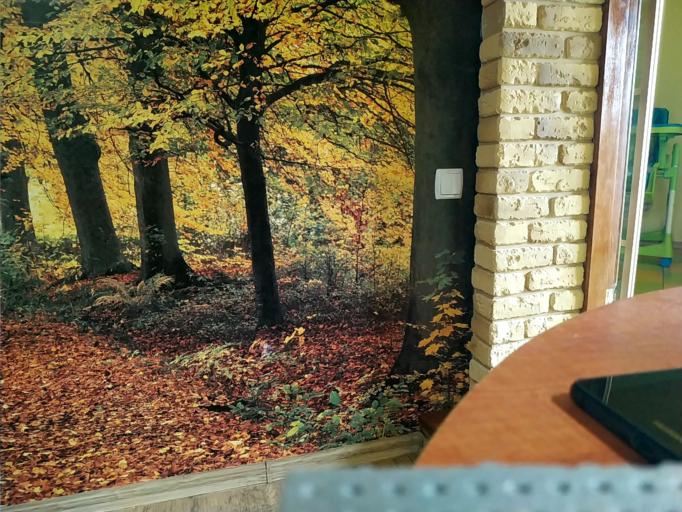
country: RU
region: Tverskaya
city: Kalashnikovo
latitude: 57.3347
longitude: 35.0973
